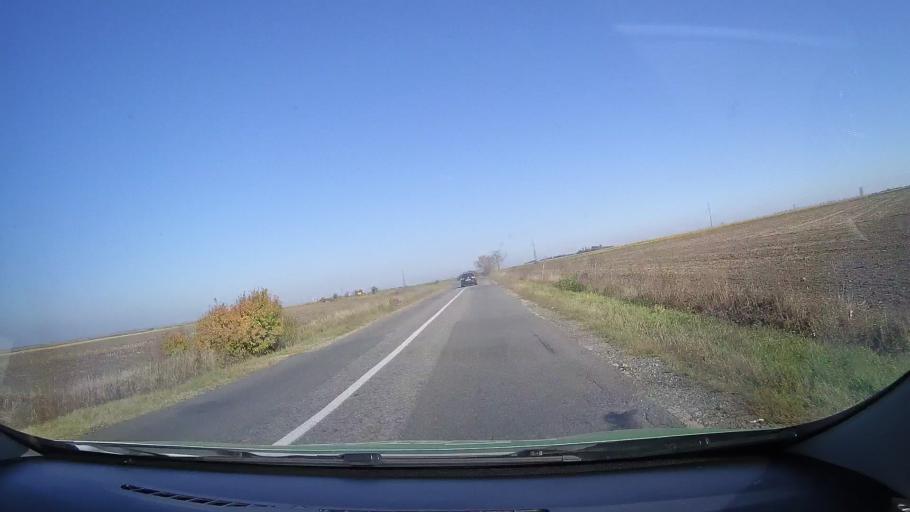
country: RO
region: Satu Mare
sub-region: Comuna Cauas
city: Cauas
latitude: 47.5984
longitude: 22.5463
